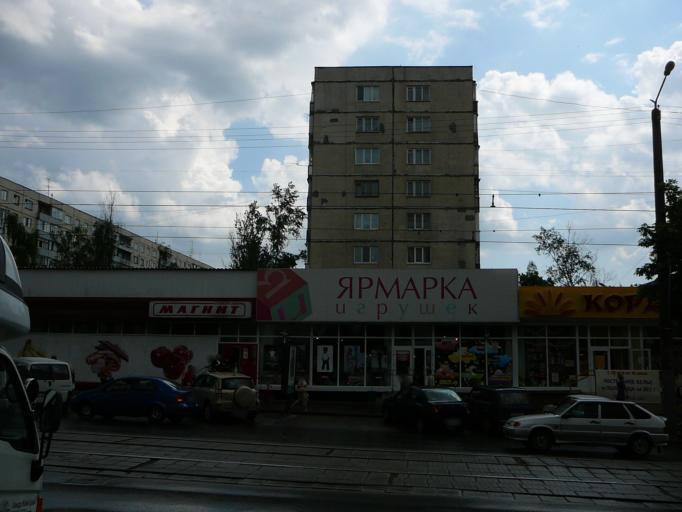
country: RU
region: Smolensk
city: Smolensk
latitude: 54.7733
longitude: 32.0364
